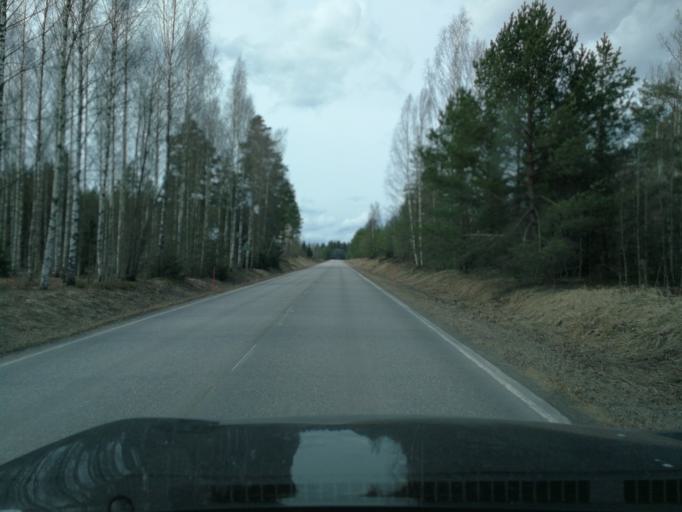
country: FI
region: Uusimaa
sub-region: Helsinki
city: Siuntio
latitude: 60.1946
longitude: 24.1958
